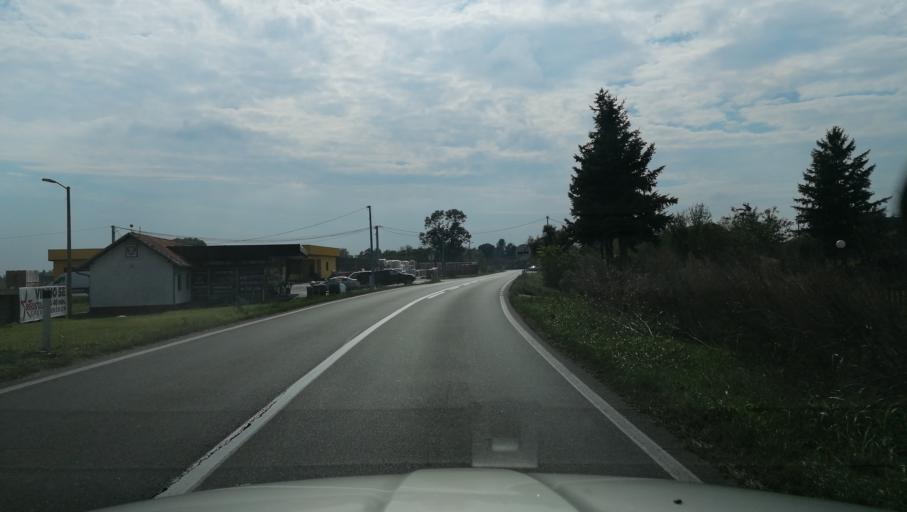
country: BA
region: Republika Srpska
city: Dvorovi
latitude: 44.8347
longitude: 19.2952
